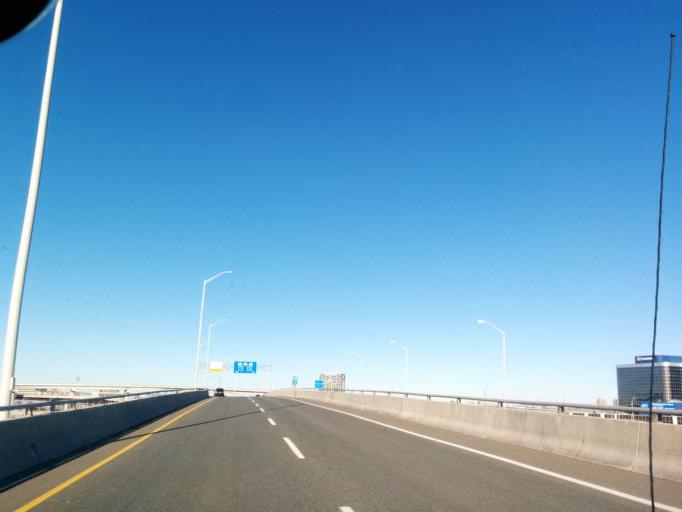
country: CA
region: Ontario
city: Etobicoke
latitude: 43.6841
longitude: -79.6102
